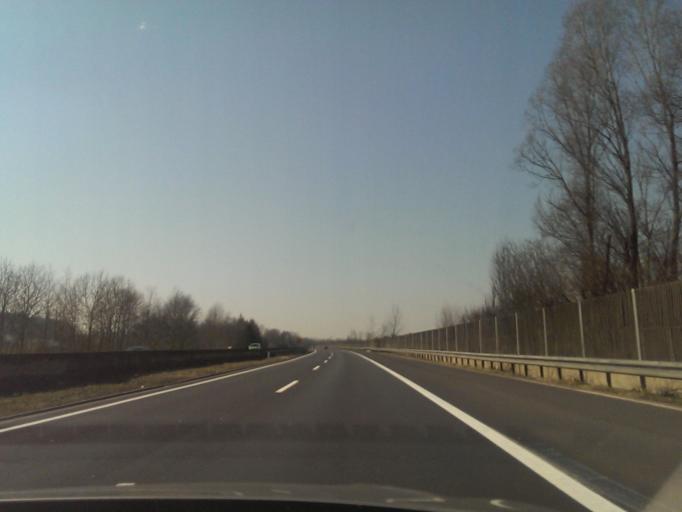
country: AT
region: Upper Austria
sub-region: Politischer Bezirk Scharding
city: Sankt Marienkirchen bei Schaerding
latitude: 48.3068
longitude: 13.4536
